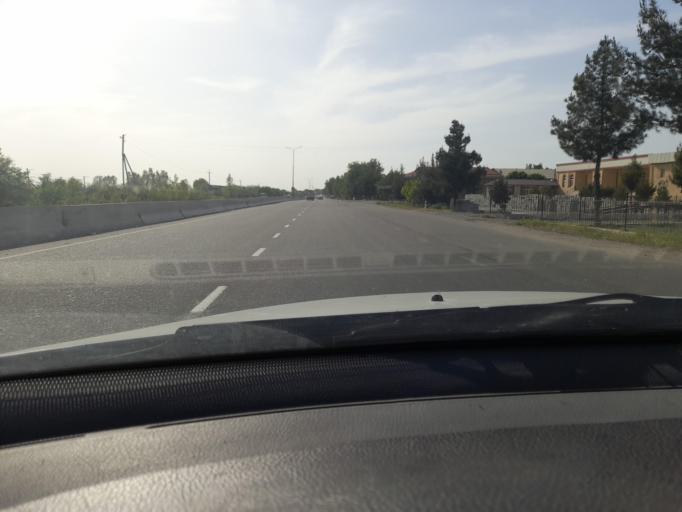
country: UZ
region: Samarqand
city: Kattaqo'rg'on
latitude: 39.9239
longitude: 66.2278
